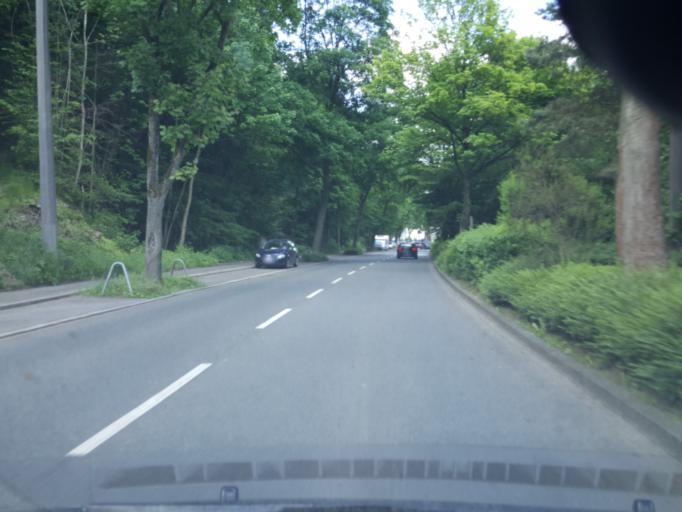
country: DE
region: North Rhine-Westphalia
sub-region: Regierungsbezirk Arnsberg
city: Hagen
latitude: 51.3372
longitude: 7.4785
